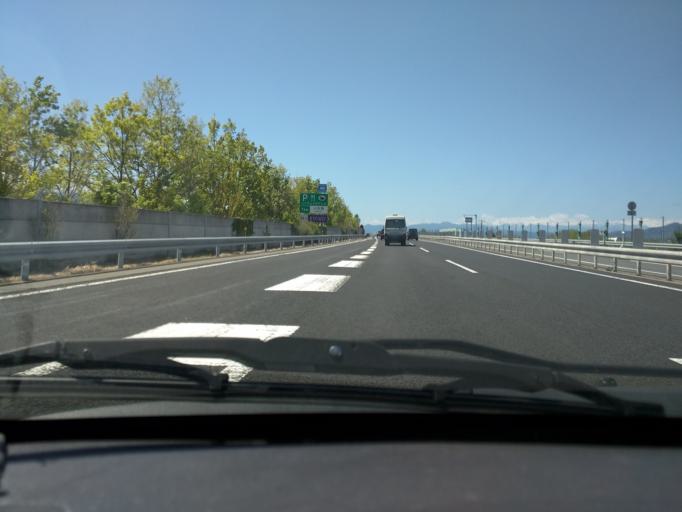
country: JP
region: Nagano
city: Suzaka
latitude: 36.7032
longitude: 138.3024
